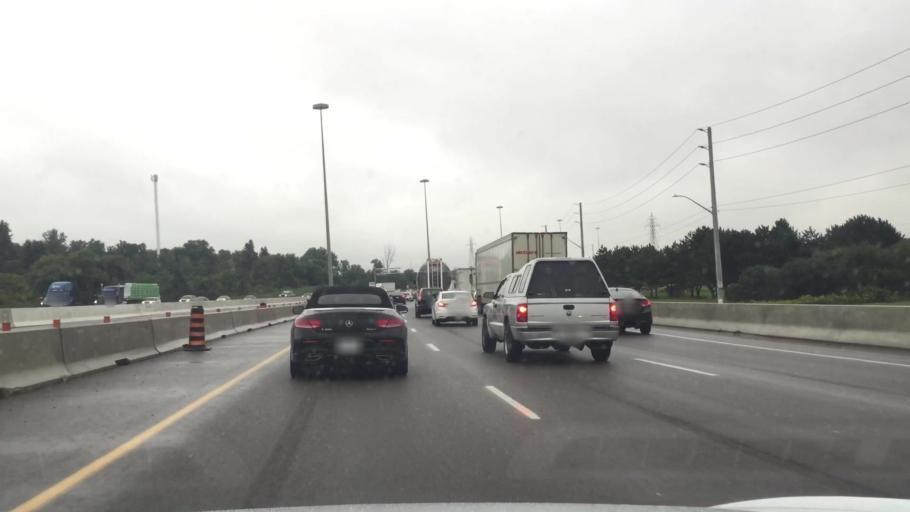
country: CA
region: Ontario
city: Cambridge
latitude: 43.4122
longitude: -80.3570
